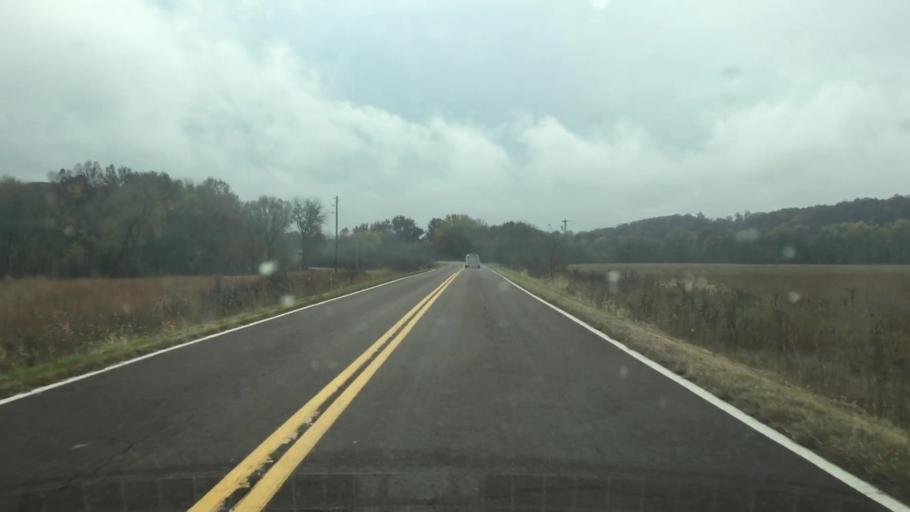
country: US
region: Missouri
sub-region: Callaway County
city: Fulton
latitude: 38.7836
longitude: -91.8542
